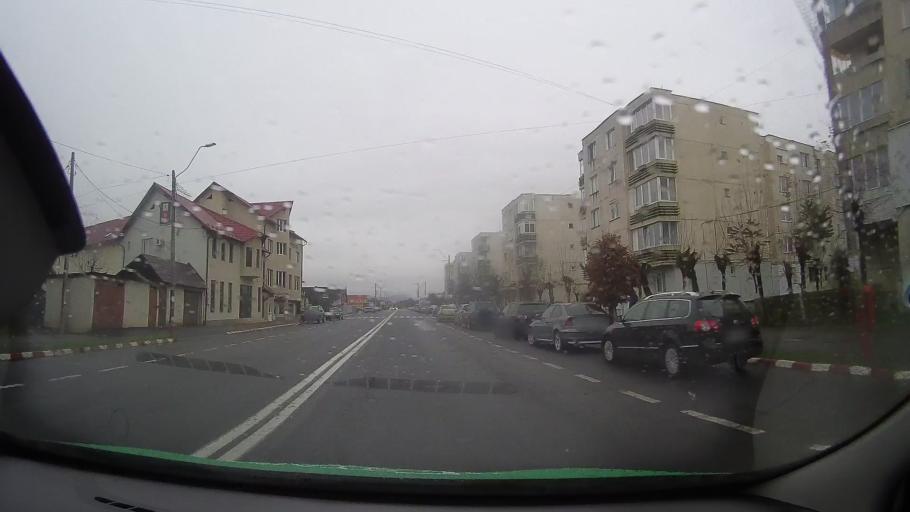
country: RO
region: Mures
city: Reghin-Sat
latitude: 46.7848
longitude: 24.7119
